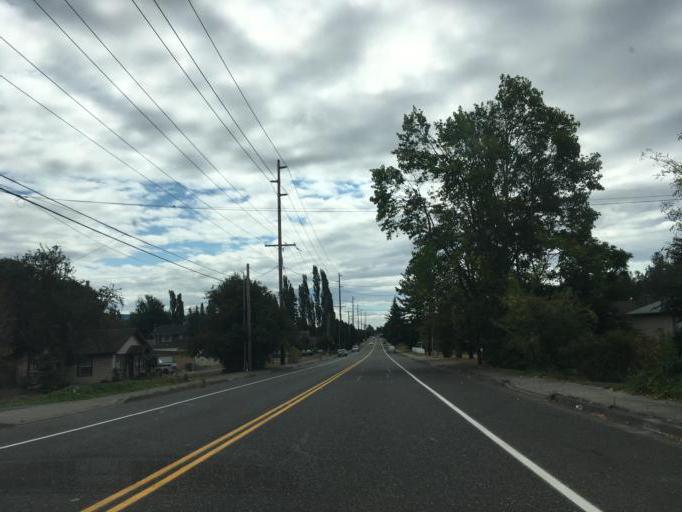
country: US
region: Washington
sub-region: Whatcom County
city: Bellingham
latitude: 48.7741
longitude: -122.5202
